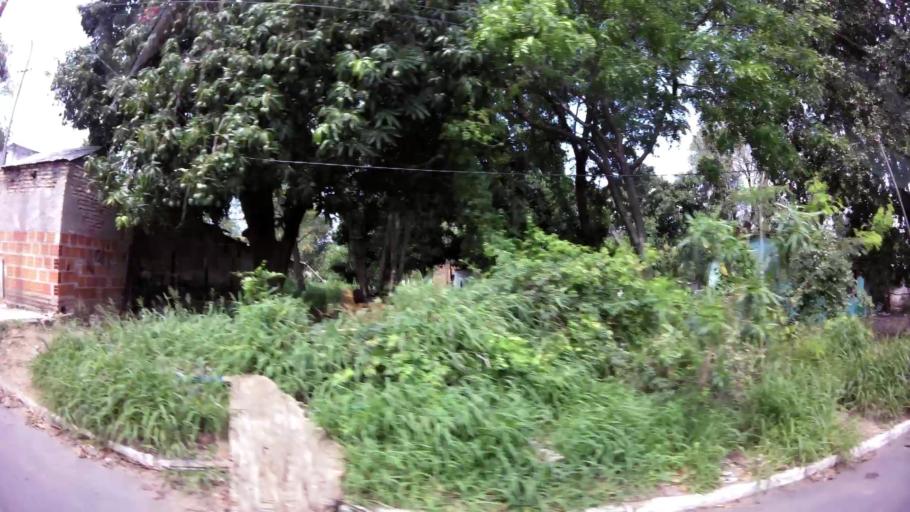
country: PY
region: Asuncion
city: Asuncion
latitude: -25.2683
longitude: -57.5844
